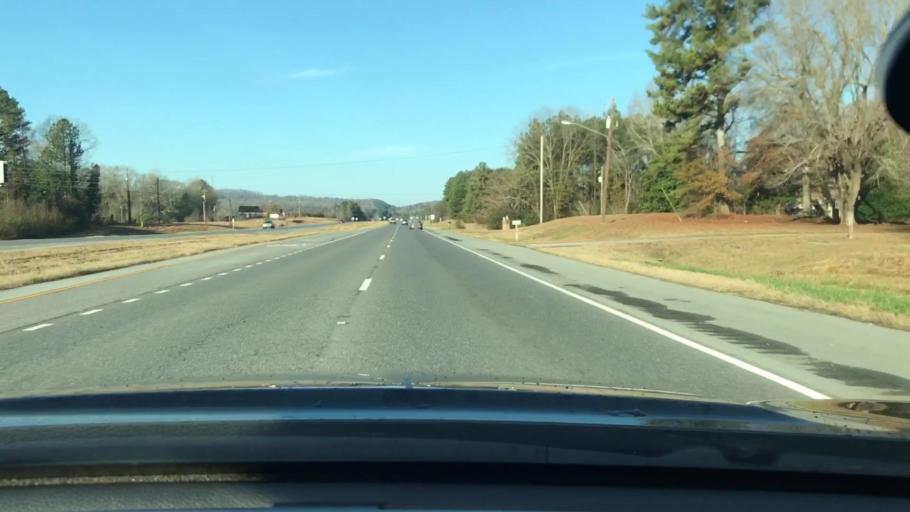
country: US
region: Alabama
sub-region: Shelby County
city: Harpersville
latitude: 33.3481
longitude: -86.4552
